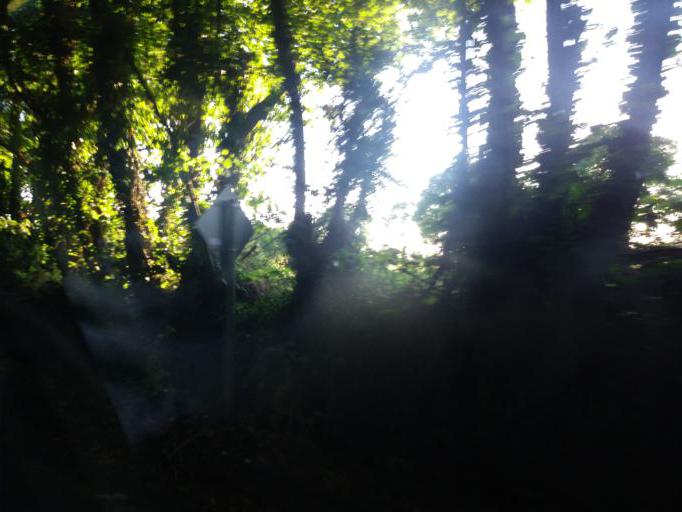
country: IE
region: Leinster
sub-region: An Mhi
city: Ashbourne
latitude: 53.5392
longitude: -6.3637
